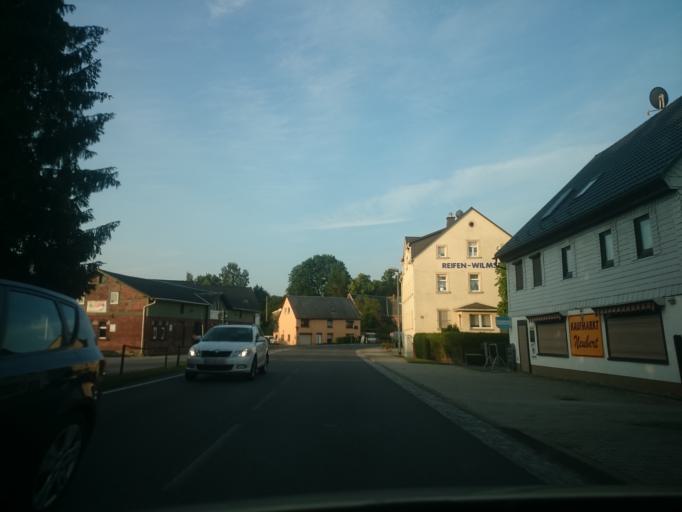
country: DE
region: Saxony
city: Grosshartmannsdorf
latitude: 50.8044
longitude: 13.3231
